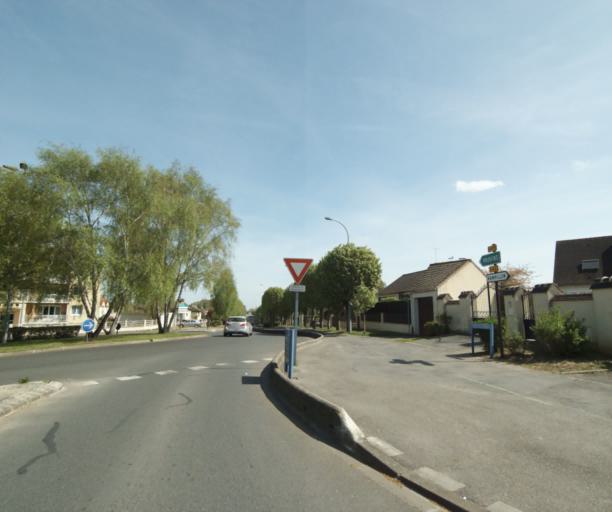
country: FR
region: Ile-de-France
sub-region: Departement de Seine-et-Marne
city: Nangis
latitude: 48.5555
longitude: 3.0193
